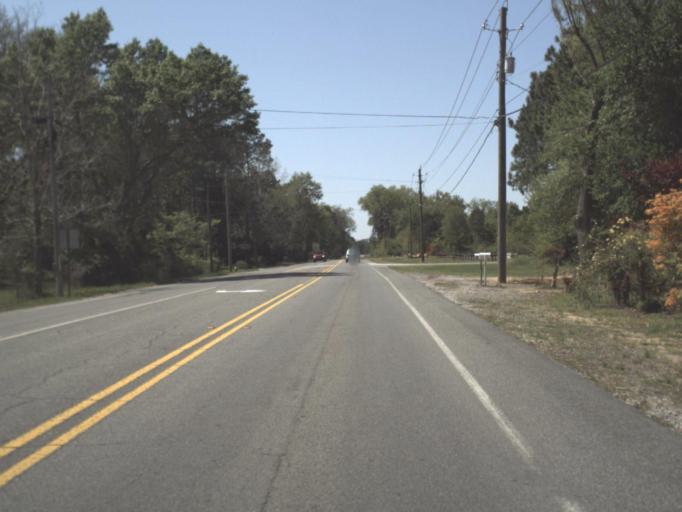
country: US
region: Florida
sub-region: Escambia County
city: Bellview
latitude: 30.5145
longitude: -87.3723
